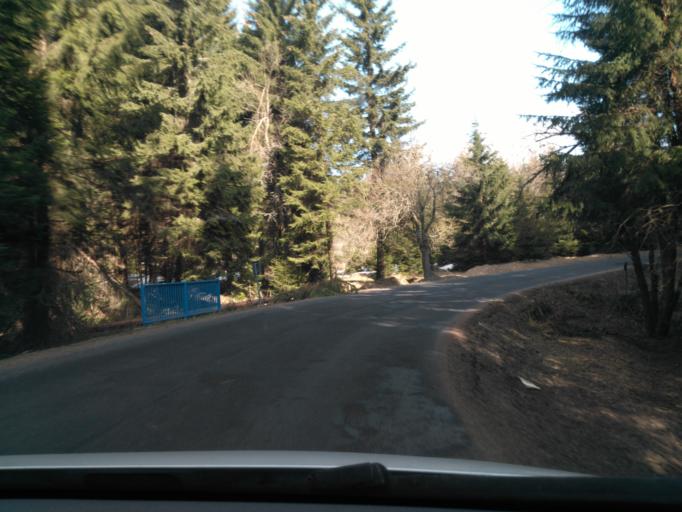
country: CZ
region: Ustecky
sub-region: Okres Chomutov
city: Kovarska
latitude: 50.4538
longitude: 13.0540
